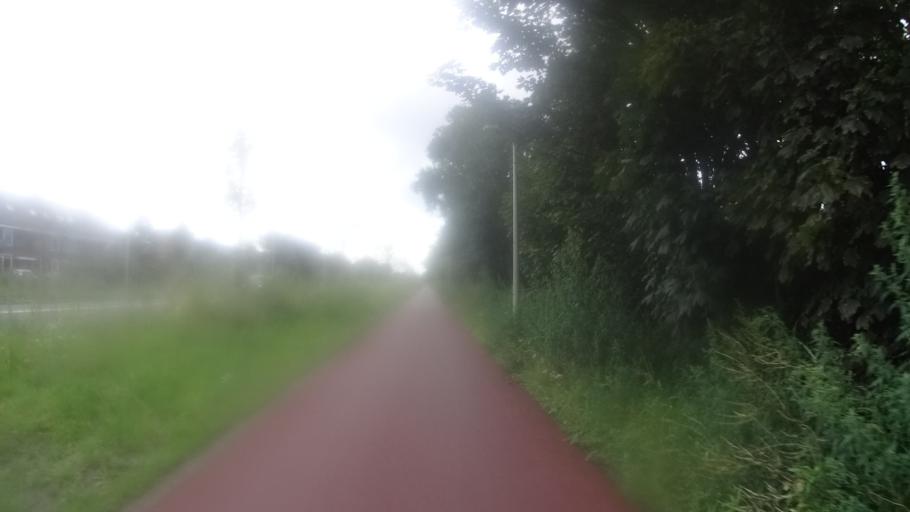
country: NL
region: South Holland
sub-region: Gemeente Westland
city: Poeldijk
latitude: 52.0696
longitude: 4.2346
